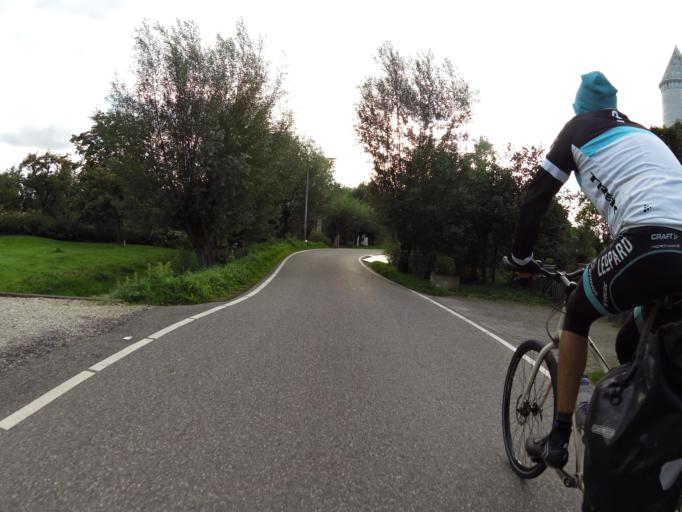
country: NL
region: South Holland
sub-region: Gemeente Nieuwkoop
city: Nieuwkoop
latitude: 52.1200
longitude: 4.7897
